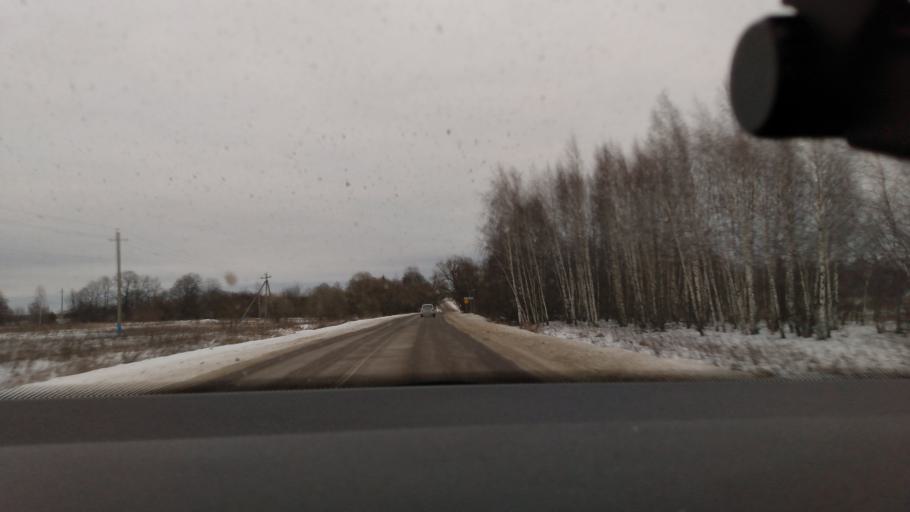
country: RU
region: Moskovskaya
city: Krasnaya Poyma
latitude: 55.1676
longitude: 39.1732
